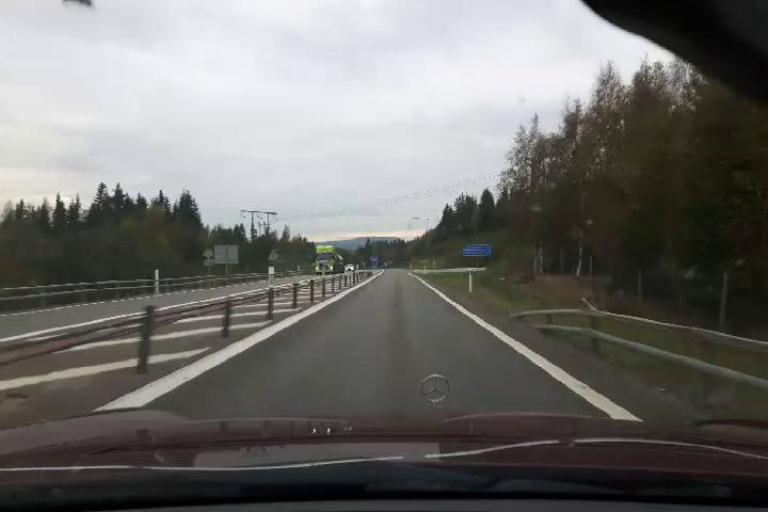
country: SE
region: Vaesternorrland
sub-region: Haernoesands Kommun
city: Haernoesand
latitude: 62.7074
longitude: 17.8705
